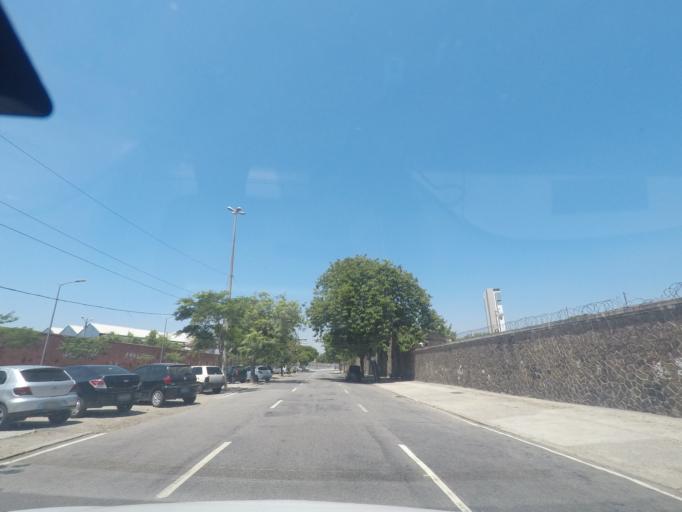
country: BR
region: Rio de Janeiro
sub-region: Rio De Janeiro
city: Rio de Janeiro
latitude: -22.9025
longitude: -43.2123
